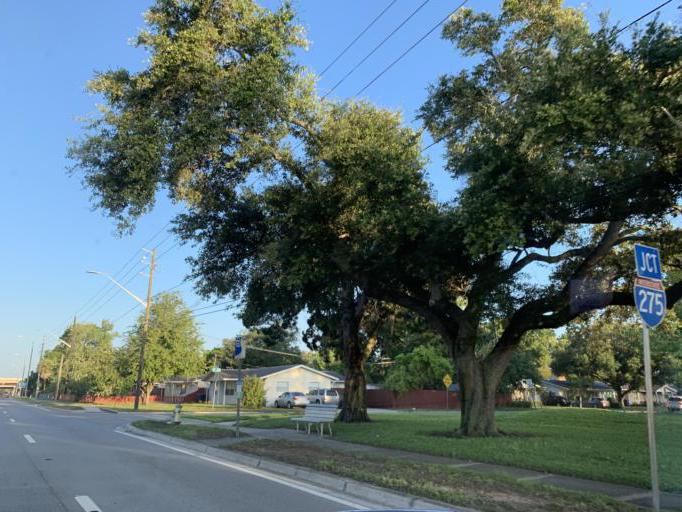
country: US
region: Florida
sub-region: Pinellas County
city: Lealman
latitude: 27.8066
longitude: -82.6588
